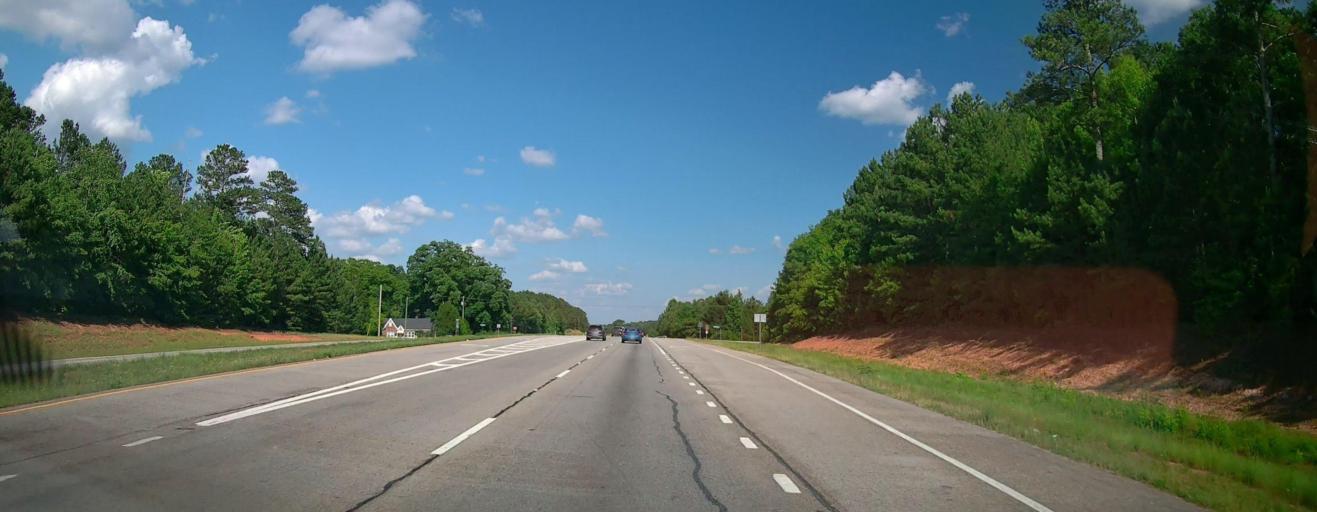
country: US
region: Georgia
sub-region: Henry County
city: Hampton
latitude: 33.3781
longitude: -84.2790
